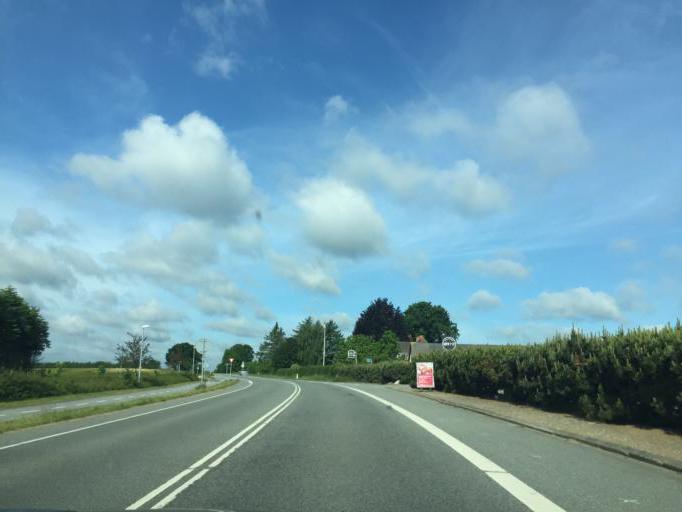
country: DK
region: South Denmark
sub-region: Fredericia Kommune
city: Taulov
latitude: 55.5334
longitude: 9.5997
